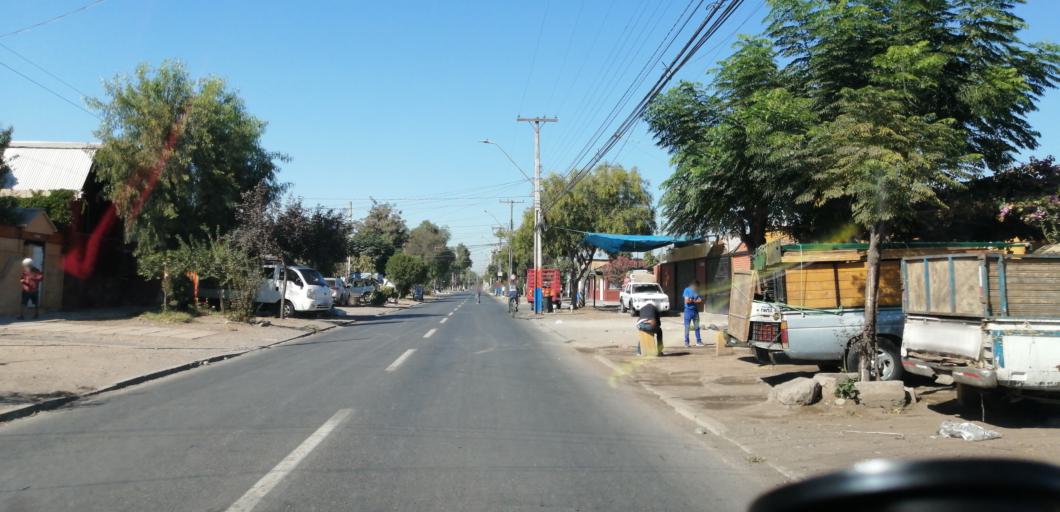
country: CL
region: Santiago Metropolitan
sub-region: Provincia de Santiago
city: Lo Prado
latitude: -33.4336
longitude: -70.7584
